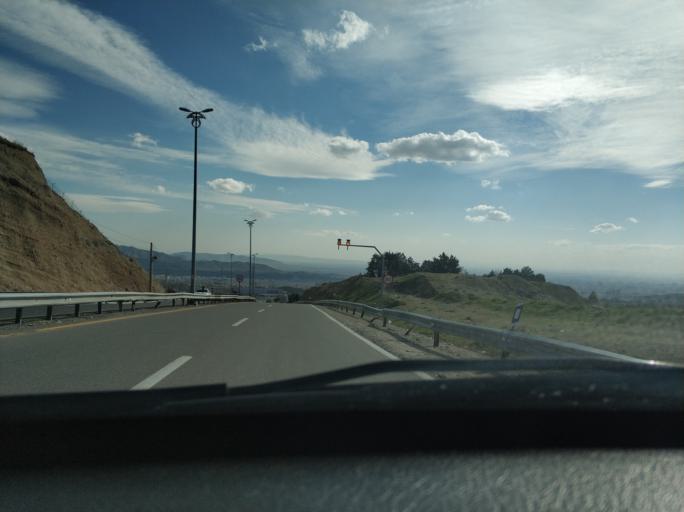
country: IR
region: Tehran
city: Tajrish
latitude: 35.7880
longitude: 51.5668
